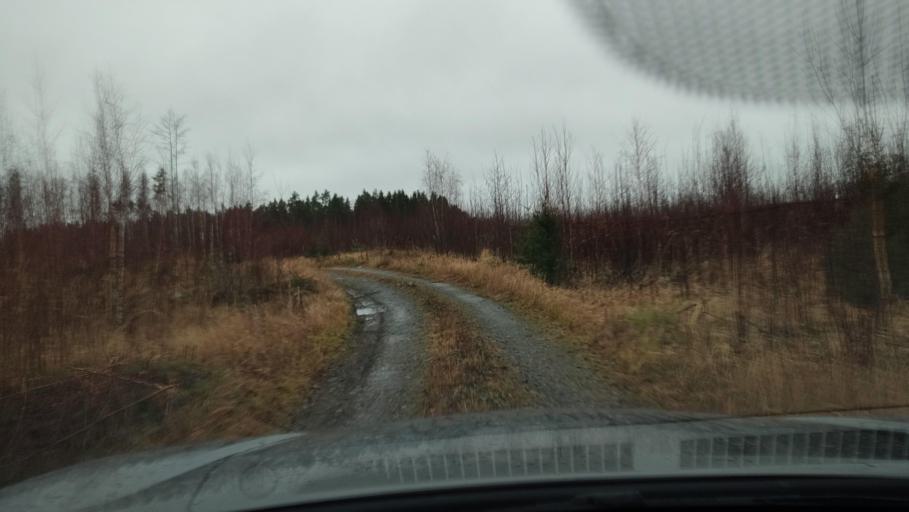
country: FI
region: Southern Ostrobothnia
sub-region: Suupohja
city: Karijoki
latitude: 62.2249
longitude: 21.5521
